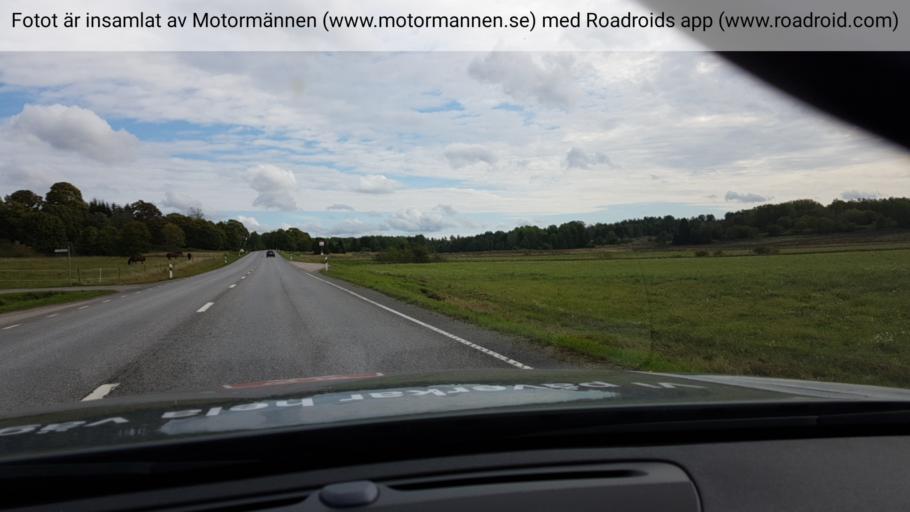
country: SE
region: Stockholm
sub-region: Norrtalje Kommun
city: Norrtalje
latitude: 59.7335
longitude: 18.5420
